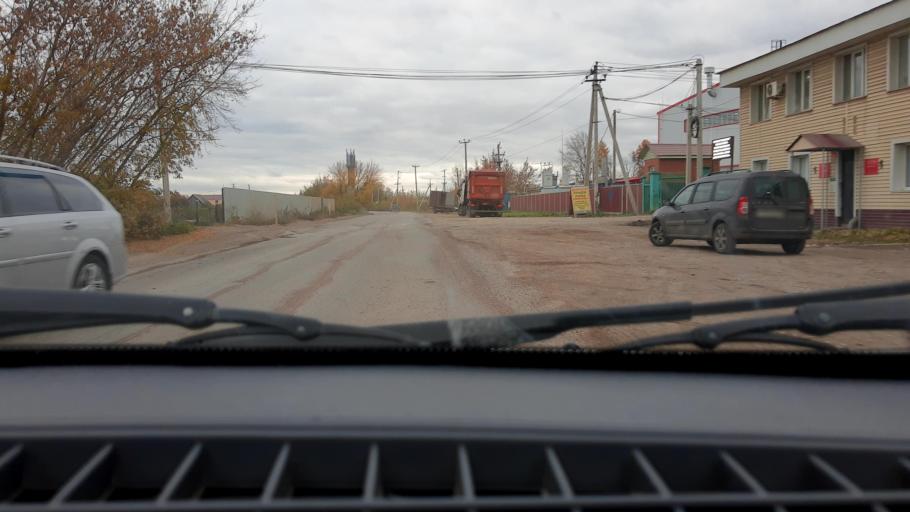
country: RU
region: Bashkortostan
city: Ufa
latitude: 54.5689
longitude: 55.9319
